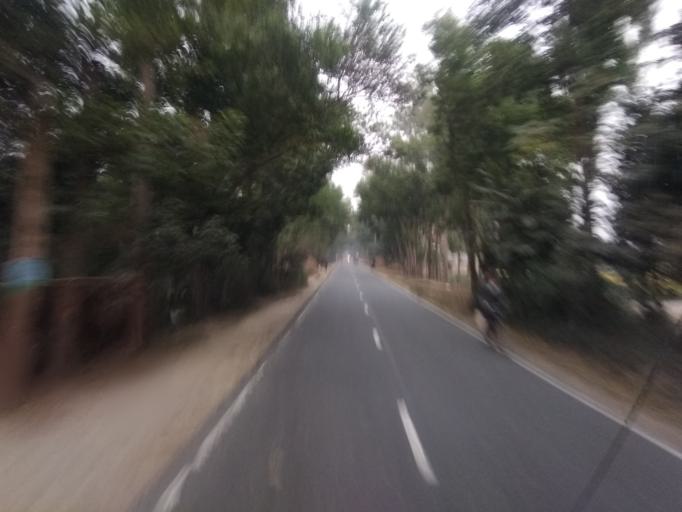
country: BD
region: Rajshahi
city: Bogra
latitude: 24.6637
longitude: 89.2707
